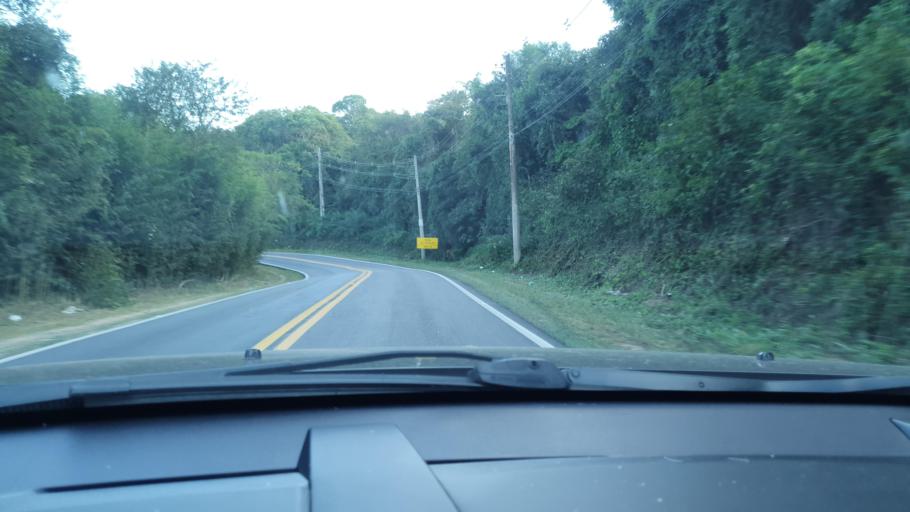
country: BR
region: Sao Paulo
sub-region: Ibiuna
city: Ibiuna
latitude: -23.6773
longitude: -47.2992
